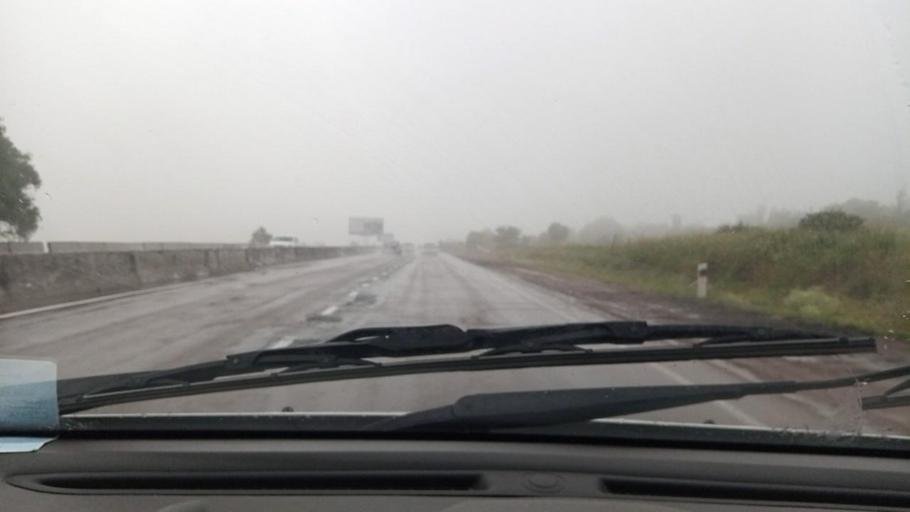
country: UZ
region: Toshkent
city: Angren
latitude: 41.0517
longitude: 70.1604
